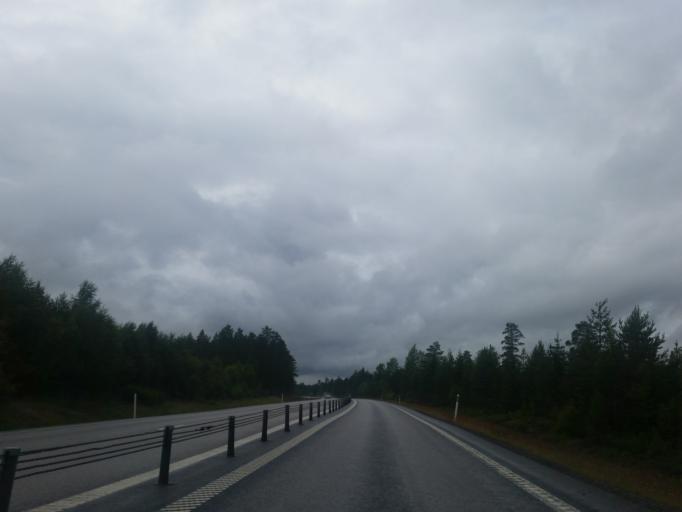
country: SE
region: Vaesterbotten
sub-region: Umea Kommun
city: Saevar
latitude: 63.9549
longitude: 20.6710
